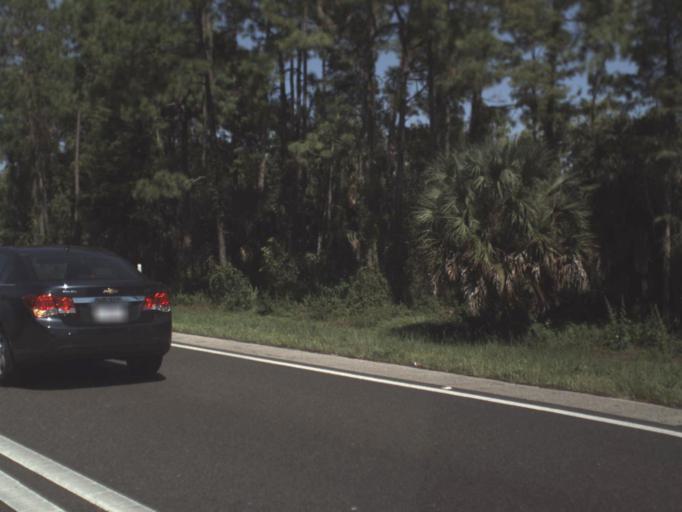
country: US
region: Florida
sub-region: Collier County
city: Vineyards
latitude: 26.2184
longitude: -81.7361
